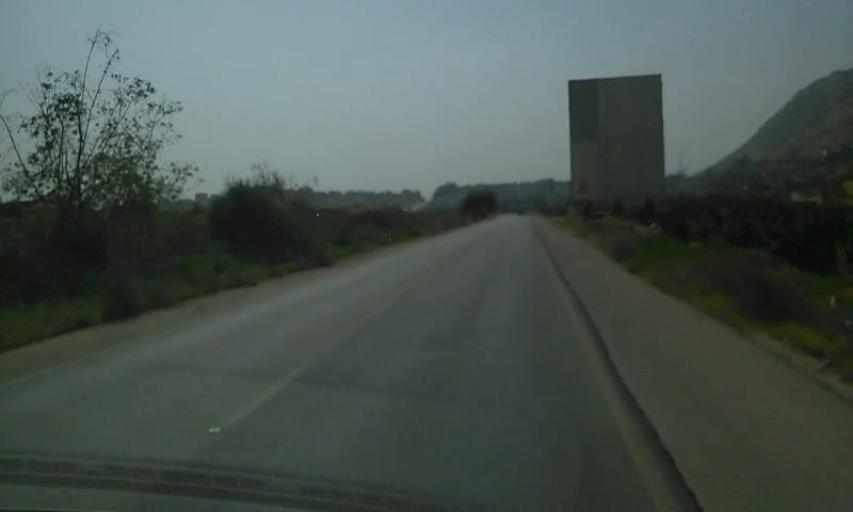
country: PS
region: West Bank
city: An Nuway`imah
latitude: 31.8852
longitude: 35.4351
